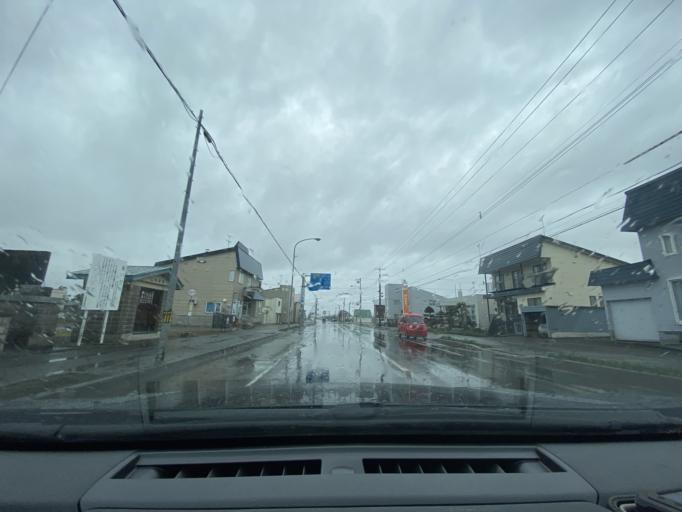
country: JP
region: Hokkaido
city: Fukagawa
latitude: 43.8089
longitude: 142.0242
